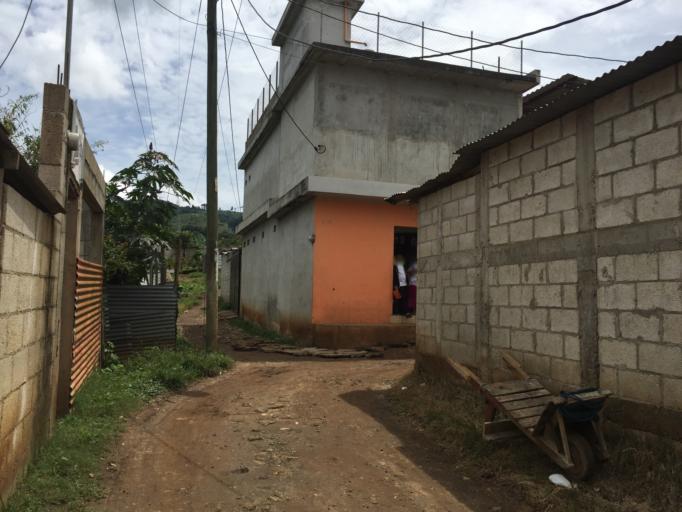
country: GT
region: Guatemala
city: Villa Canales
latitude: 14.4804
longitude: -90.5229
